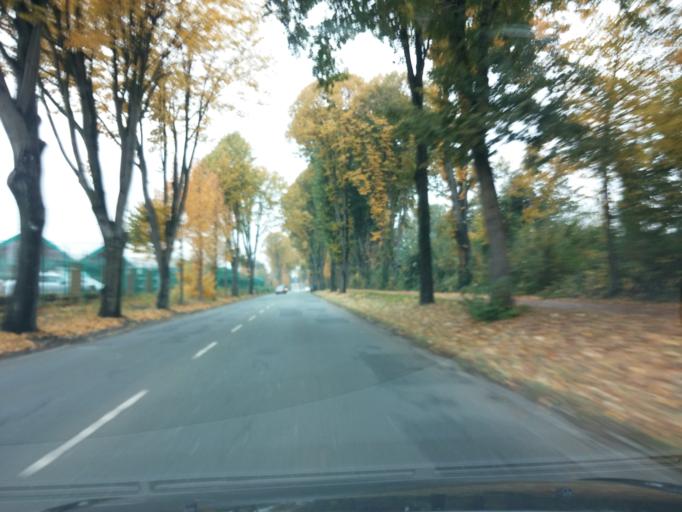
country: DE
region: North Rhine-Westphalia
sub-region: Regierungsbezirk Munster
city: Gladbeck
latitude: 51.5808
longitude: 7.0087
